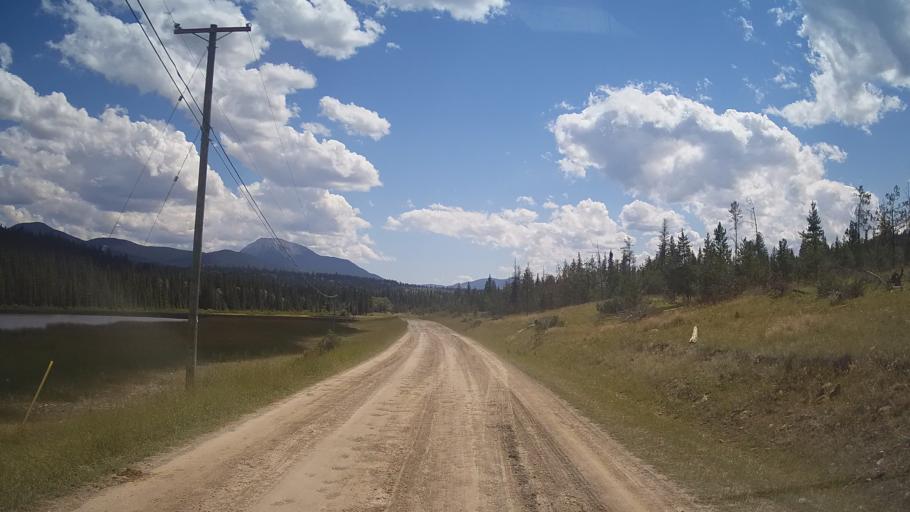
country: CA
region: British Columbia
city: Lillooet
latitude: 51.2980
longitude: -121.9818
